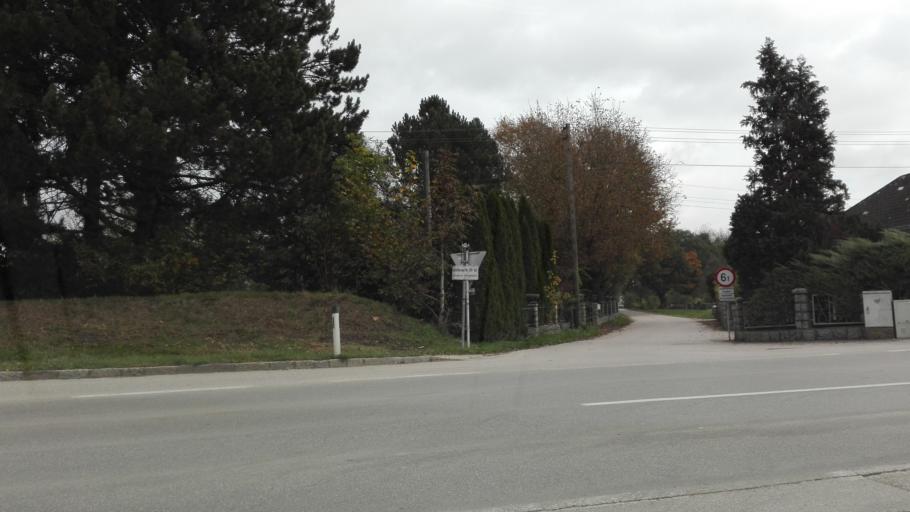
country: AT
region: Upper Austria
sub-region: Politischer Bezirk Urfahr-Umgebung
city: Feldkirchen an der Donau
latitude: 48.3290
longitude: 14.0094
